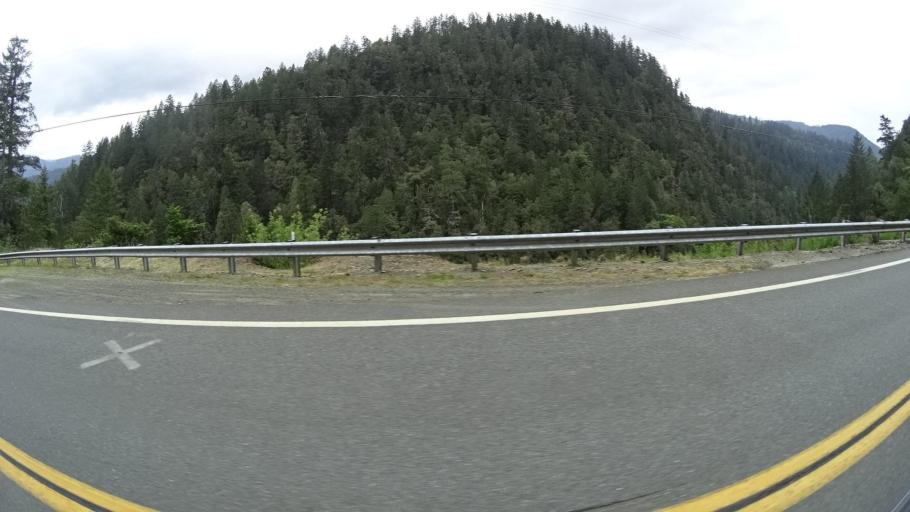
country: US
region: California
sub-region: Humboldt County
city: Willow Creek
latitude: 41.1094
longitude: -123.6860
